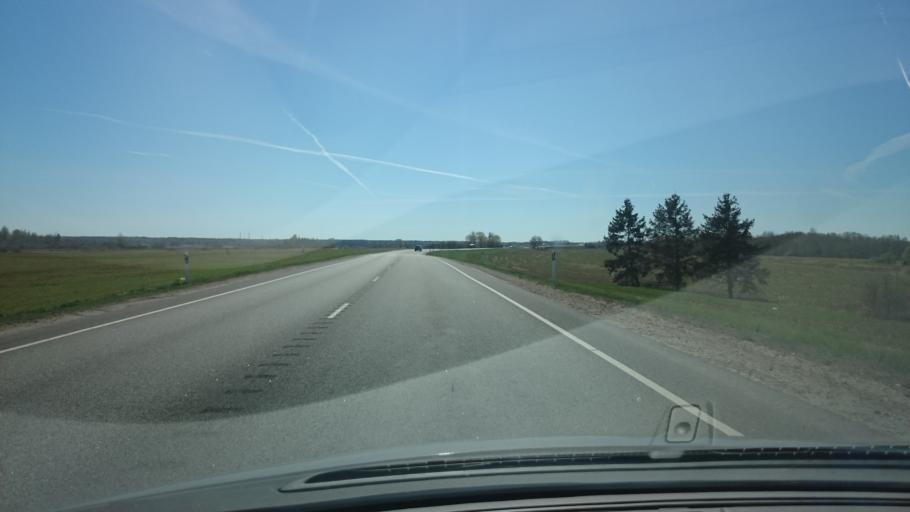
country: EE
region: Ida-Virumaa
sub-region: Narva-Joesuu linn
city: Narva-Joesuu
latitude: 59.4031
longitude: 28.0165
